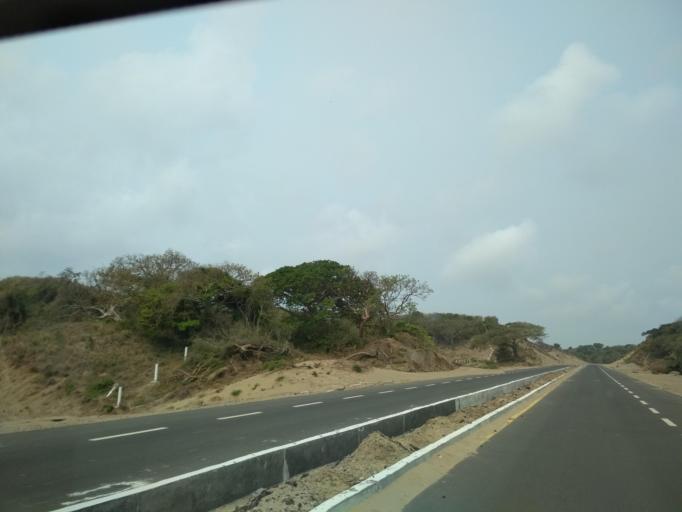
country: MX
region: Veracruz
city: Anton Lizardo
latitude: 19.0439
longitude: -95.9882
